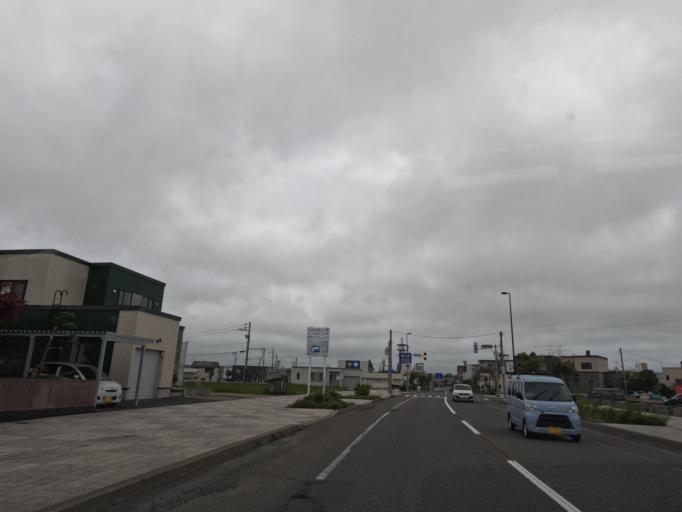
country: JP
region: Hokkaido
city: Tobetsu
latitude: 43.2155
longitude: 141.5164
